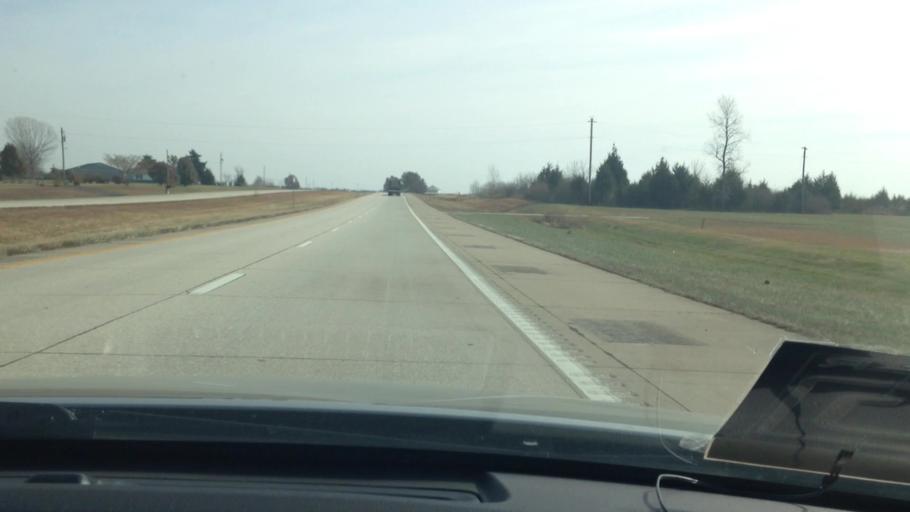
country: US
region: Missouri
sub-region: Henry County
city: Clinton
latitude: 38.4319
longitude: -93.9293
